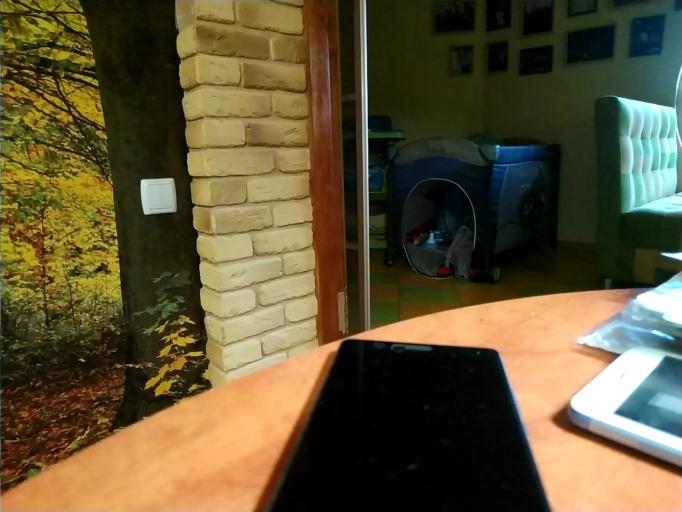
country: RU
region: Orjol
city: Znamenskoye
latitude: 53.5400
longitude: 35.4922
